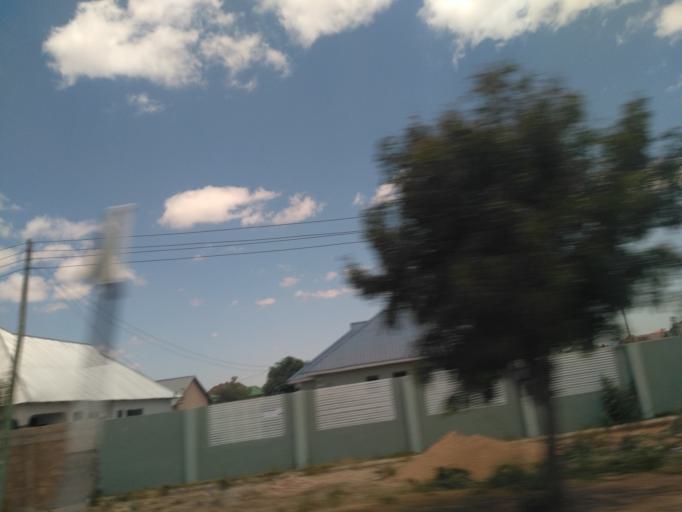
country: TZ
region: Dodoma
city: Kisasa
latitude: -6.1808
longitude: 35.7934
